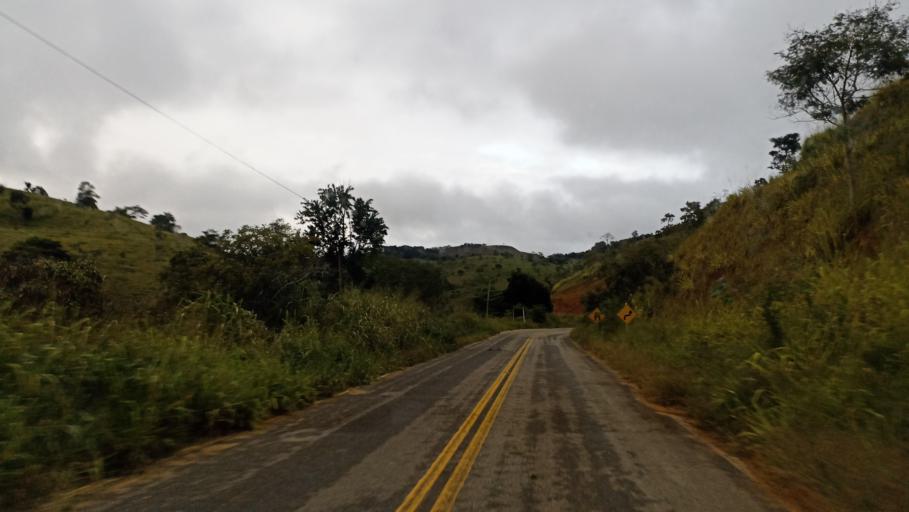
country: BR
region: Bahia
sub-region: Itanhem
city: Itanhem
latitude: -16.6956
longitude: -40.5083
